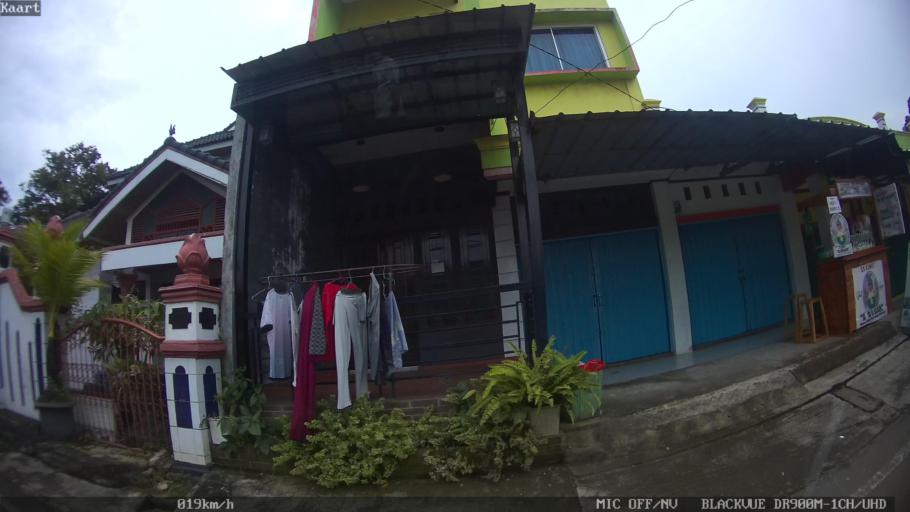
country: ID
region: Lampung
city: Kedaton
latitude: -5.3815
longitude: 105.2495
